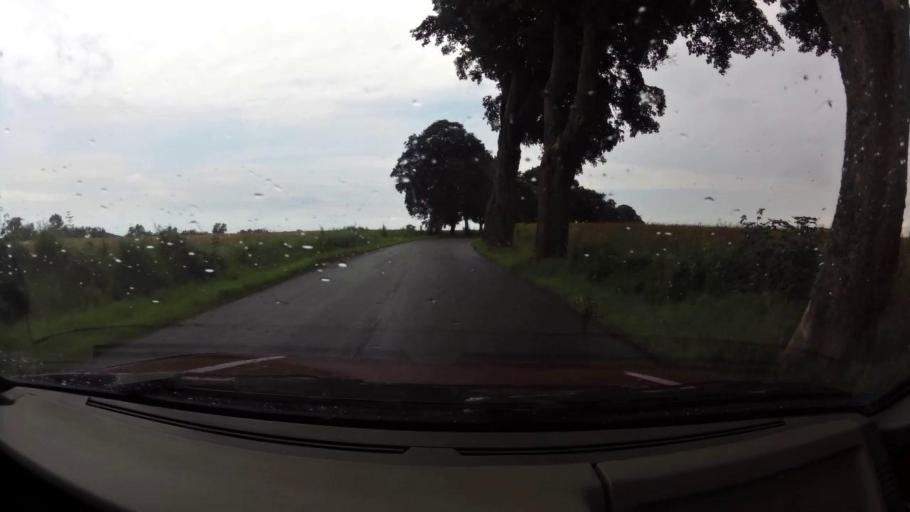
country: PL
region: West Pomeranian Voivodeship
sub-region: Koszalin
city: Koszalin
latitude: 54.1400
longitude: 16.1171
